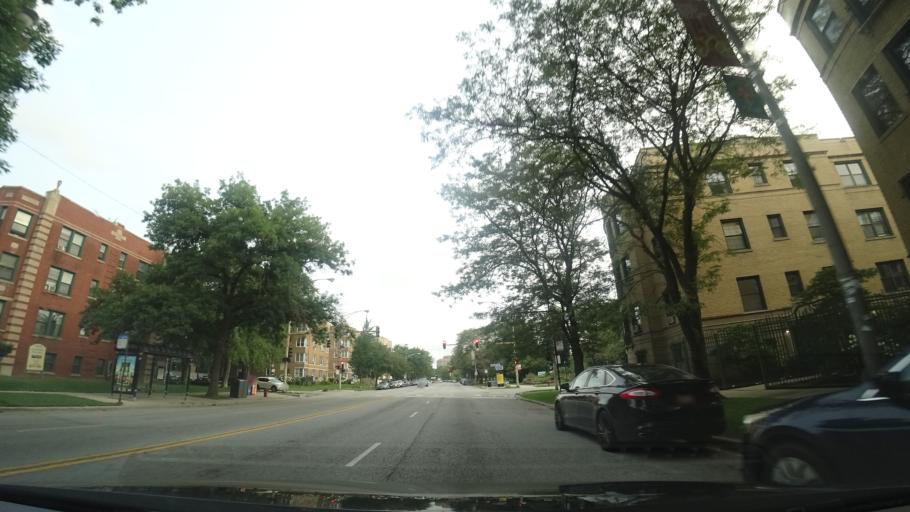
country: US
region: Illinois
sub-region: Cook County
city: Evanston
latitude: 42.0100
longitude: -87.6623
